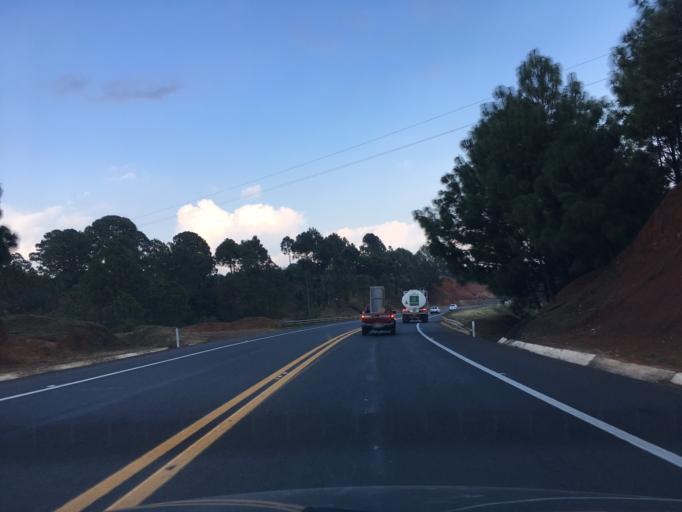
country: MX
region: Michoacan
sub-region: Uruapan
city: Toreo Bajo (El Toreo Bajo)
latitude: 19.4212
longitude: -101.9883
